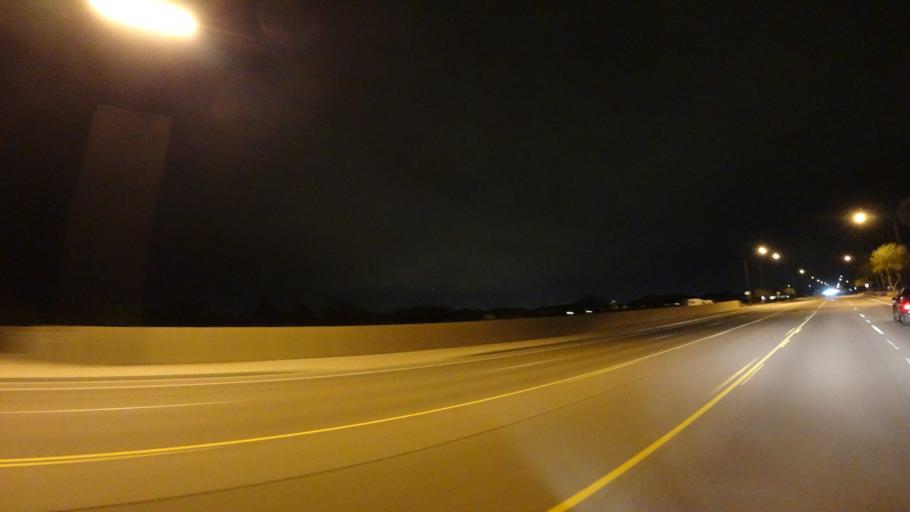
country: US
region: Arizona
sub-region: Maricopa County
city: Queen Creek
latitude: 33.2364
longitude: -111.7380
